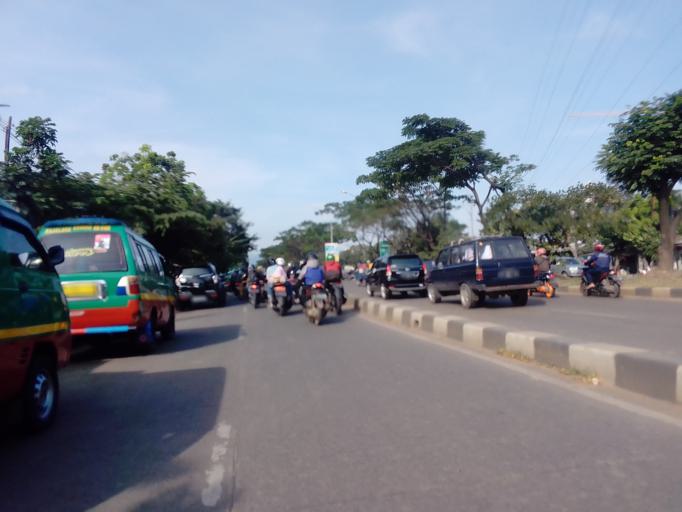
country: ID
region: West Java
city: Cileunyi
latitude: -6.9359
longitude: 107.7066
